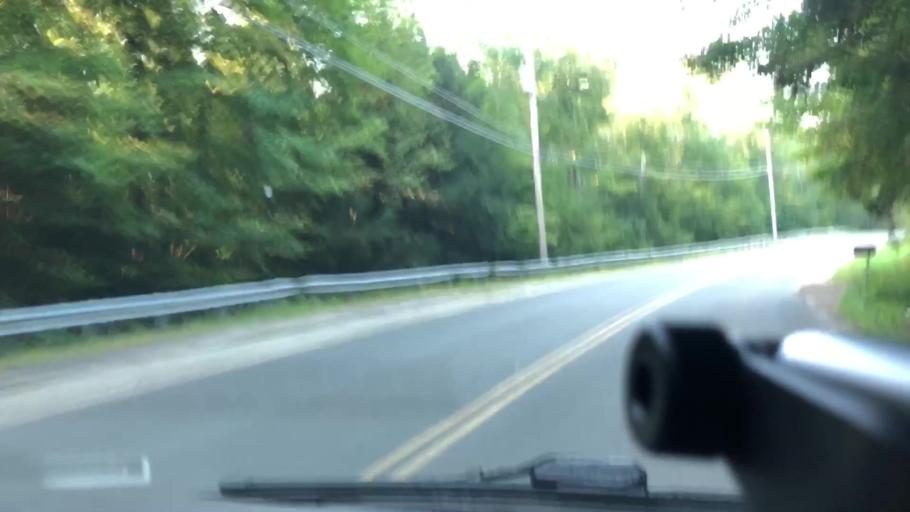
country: US
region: Massachusetts
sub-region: Franklin County
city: Ashfield
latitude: 42.4972
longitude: -72.8533
